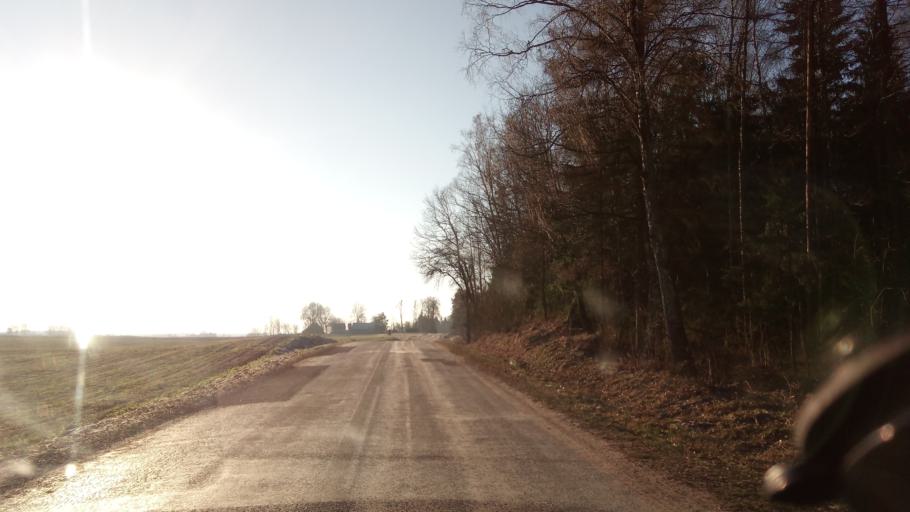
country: LT
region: Alytaus apskritis
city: Druskininkai
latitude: 54.1293
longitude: 24.0024
